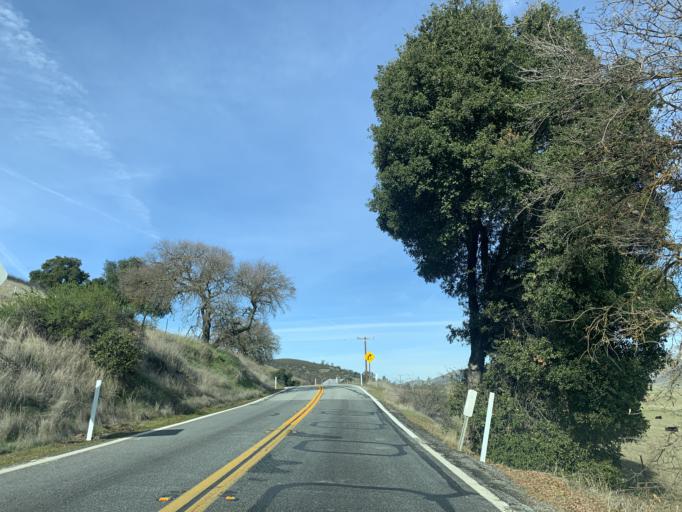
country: US
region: California
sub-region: Monterey County
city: Soledad
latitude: 36.5650
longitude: -121.1814
